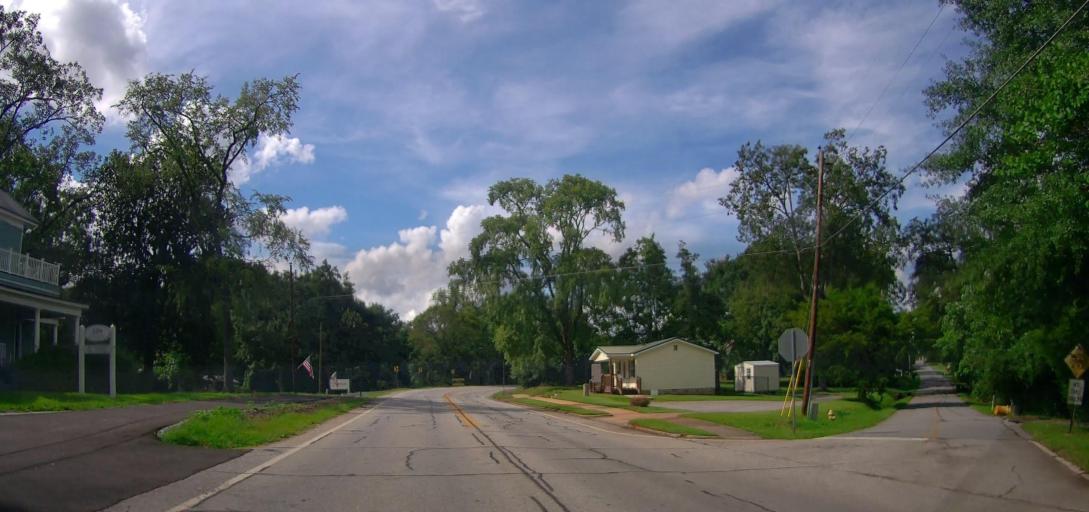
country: US
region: Georgia
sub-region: Harris County
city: Hamilton
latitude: 32.7547
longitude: -84.8743
